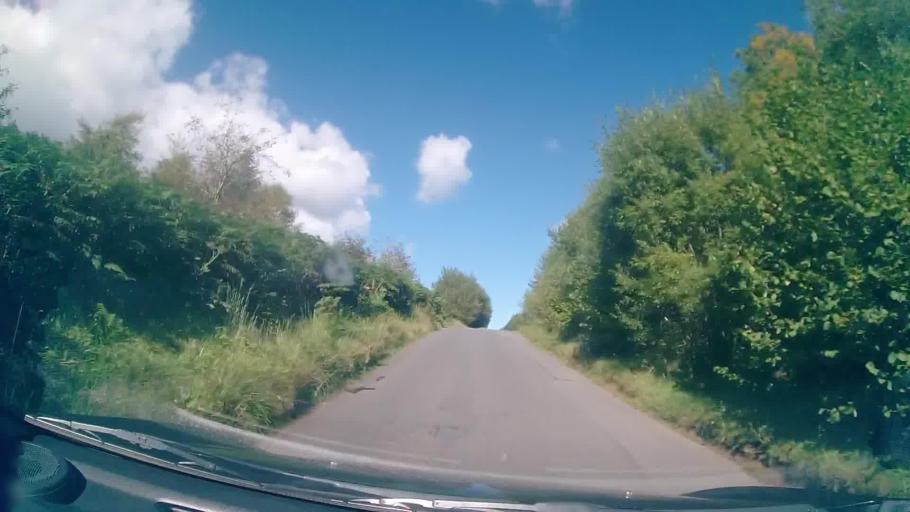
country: GB
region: Wales
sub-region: Merthyr Tydfil County Borough
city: Merthyr Tydfil
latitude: 51.8409
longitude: -3.3822
